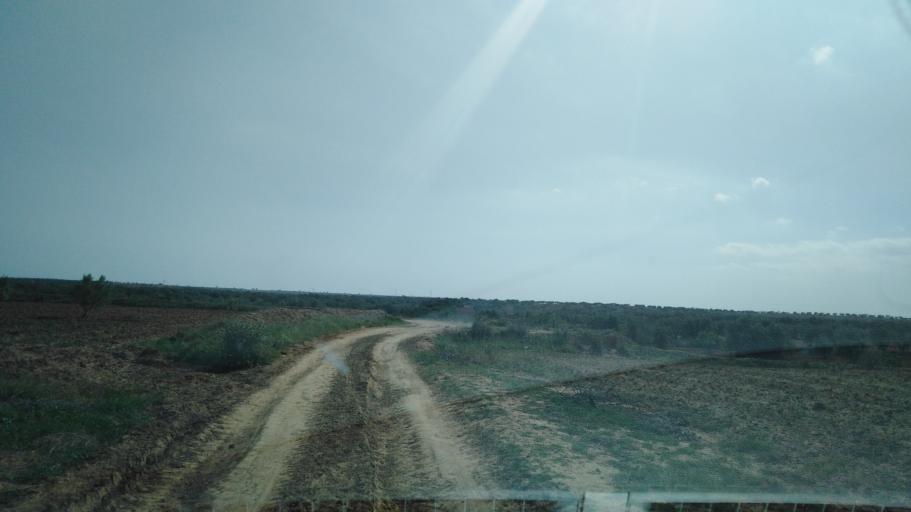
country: TN
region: Safaqis
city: Bi'r `Ali Bin Khalifah
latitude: 34.7811
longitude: 10.3642
